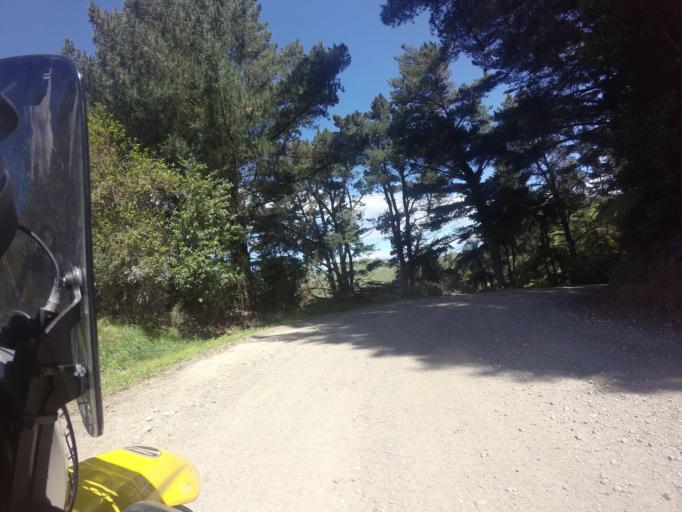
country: NZ
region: Hawke's Bay
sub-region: Wairoa District
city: Wairoa
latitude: -38.9772
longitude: 177.7039
